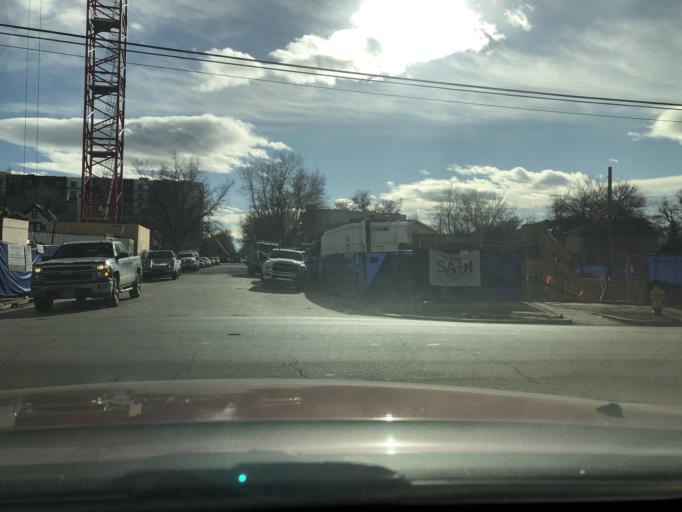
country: US
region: Colorado
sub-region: Denver County
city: Denver
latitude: 39.7449
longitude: -104.9721
